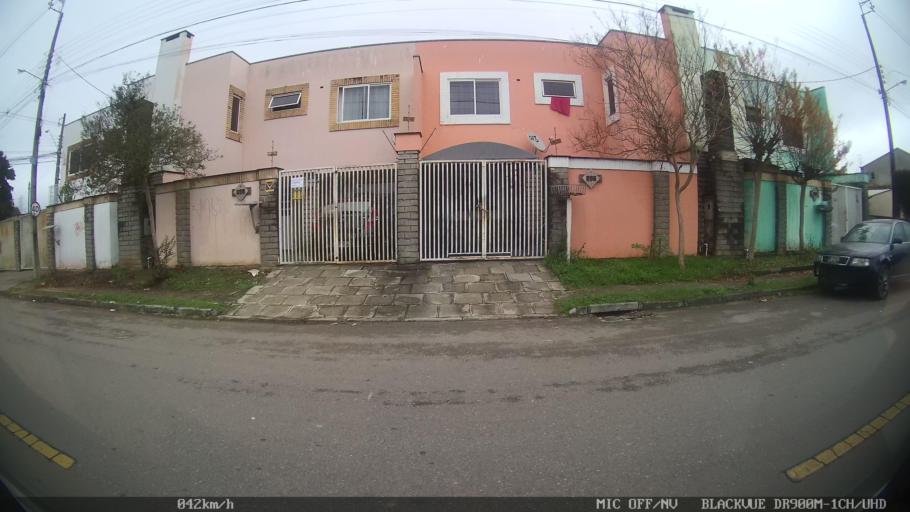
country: BR
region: Parana
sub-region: Sao Jose Dos Pinhais
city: Sao Jose dos Pinhais
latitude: -25.6018
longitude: -49.1695
